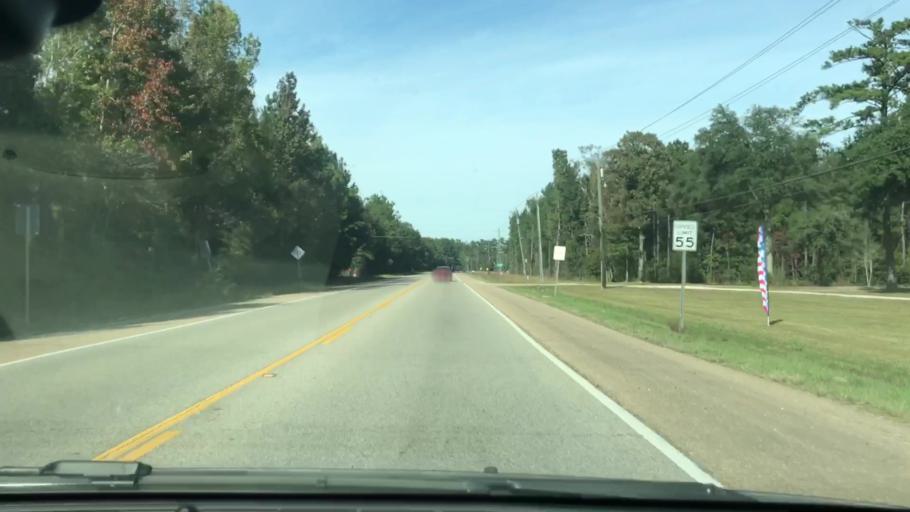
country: US
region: Louisiana
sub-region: Saint Tammany Parish
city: Pearl River
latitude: 30.3933
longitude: -89.7618
